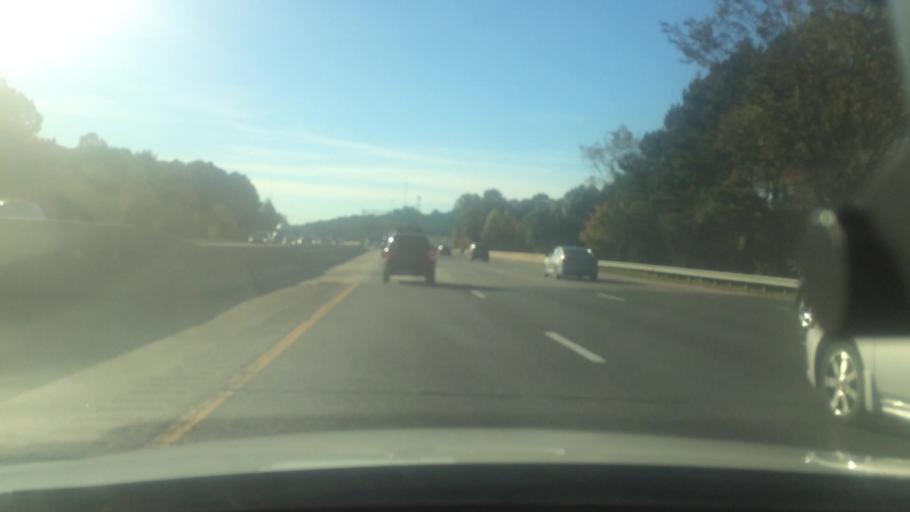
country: US
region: North Carolina
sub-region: Durham County
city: Durham
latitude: 35.9095
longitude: -78.9293
